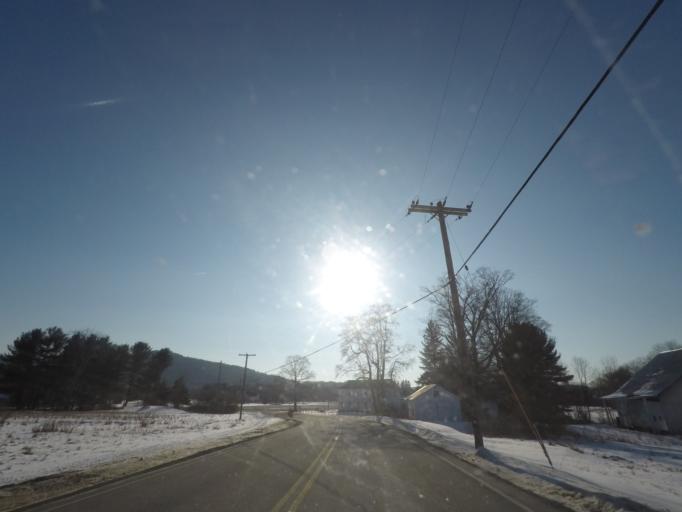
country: US
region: Massachusetts
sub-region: Berkshire County
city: Richmond
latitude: 42.4969
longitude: -73.4406
